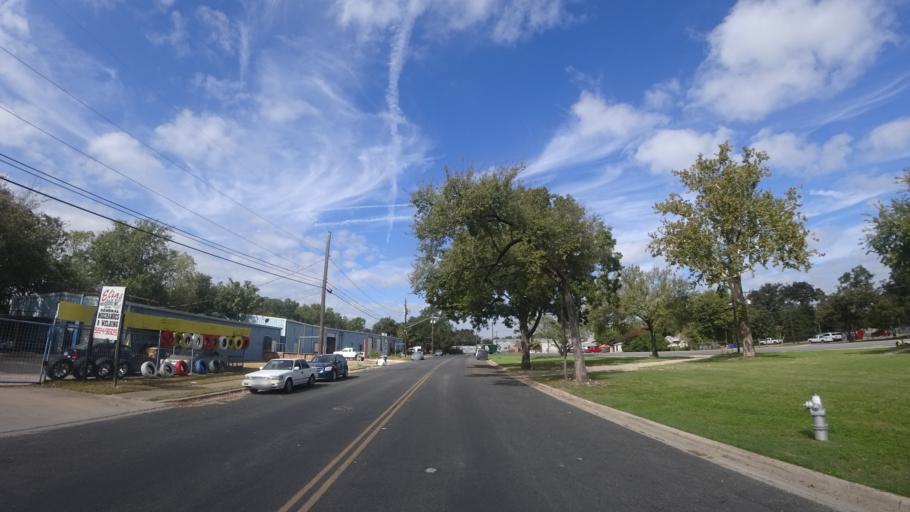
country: US
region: Texas
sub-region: Travis County
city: Austin
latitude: 30.2512
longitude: -97.7027
